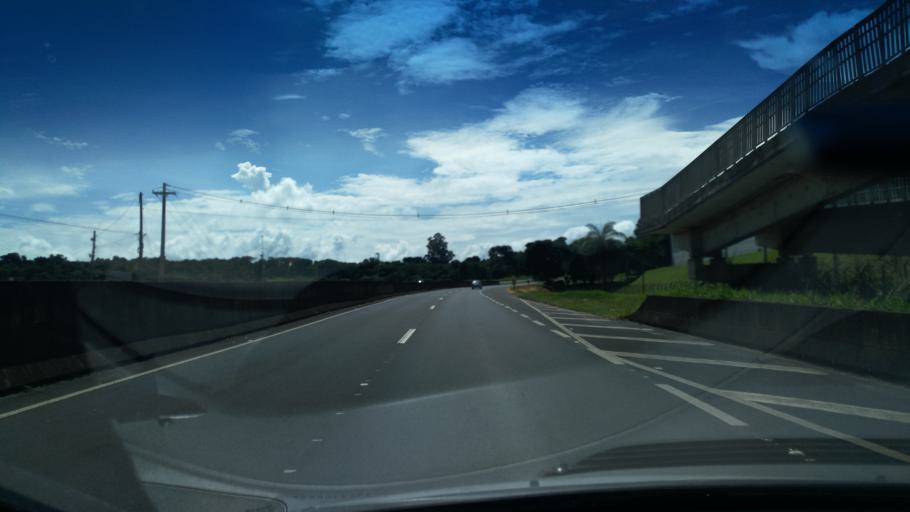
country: BR
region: Sao Paulo
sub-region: Santo Antonio Do Jardim
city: Espirito Santo do Pinhal
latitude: -22.1860
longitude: -46.7649
